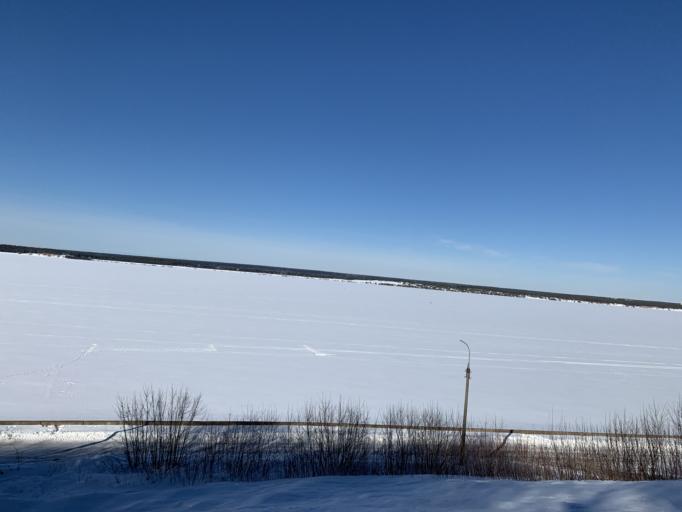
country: RU
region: Chuvashia
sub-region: Cheboksarskiy Rayon
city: Cheboksary
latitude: 56.1500
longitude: 47.2714
